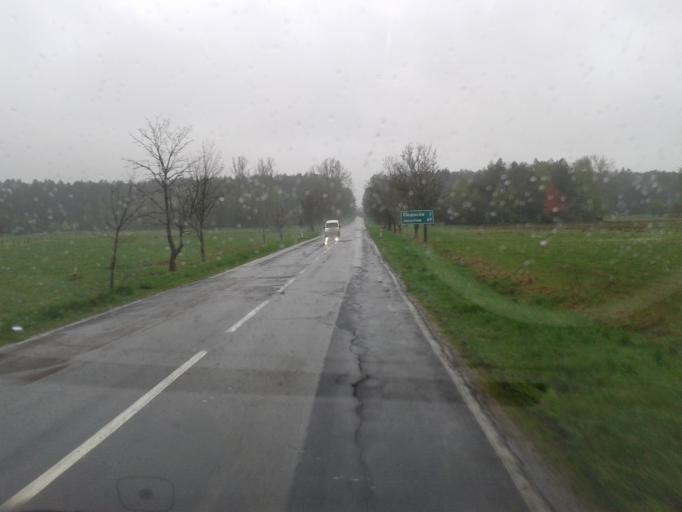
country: PL
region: Subcarpathian Voivodeship
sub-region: Powiat lubaczowski
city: Cieszanow
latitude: 50.2738
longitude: 23.1517
